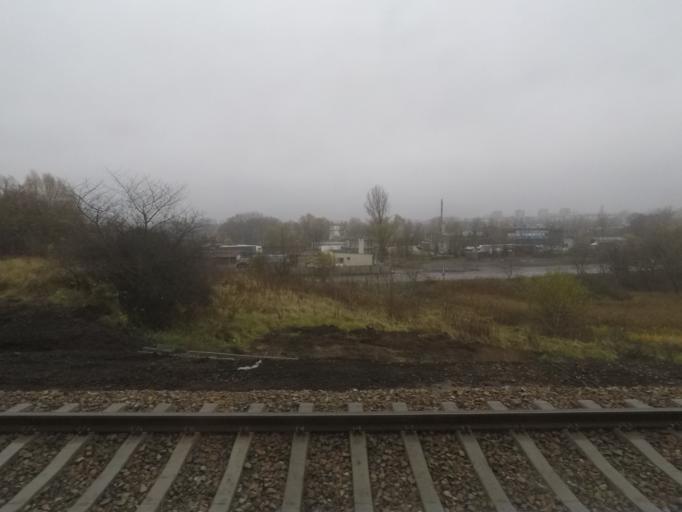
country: PL
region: Lesser Poland Voivodeship
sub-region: Powiat krakowski
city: Michalowice
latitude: 50.0938
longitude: 20.0376
